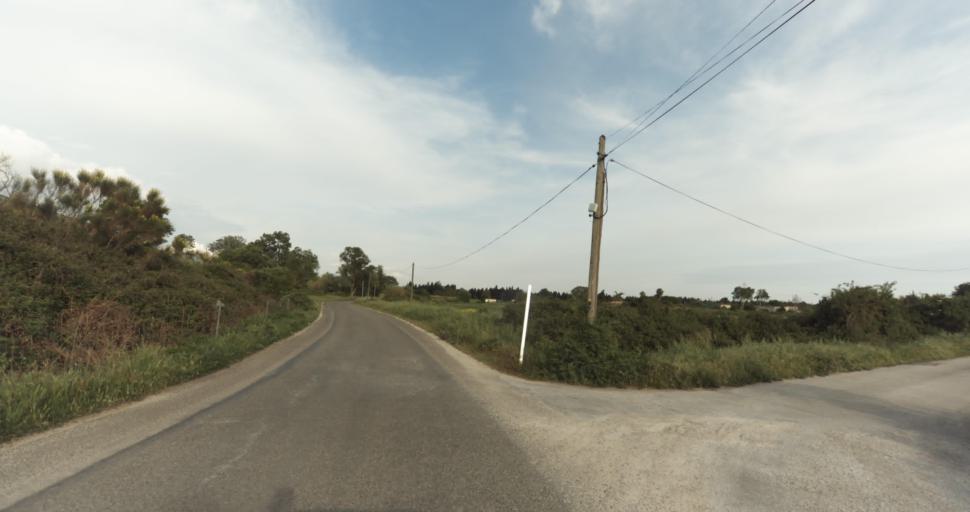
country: FR
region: Languedoc-Roussillon
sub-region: Departement du Gard
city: Nimes
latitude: 43.8073
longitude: 4.3504
